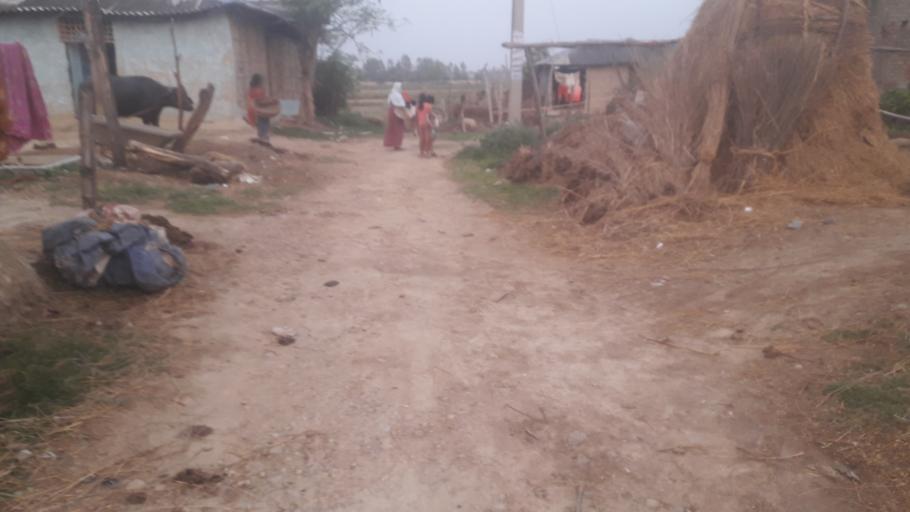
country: NP
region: Eastern Region
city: Siraha
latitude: 26.6554
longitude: 86.1962
